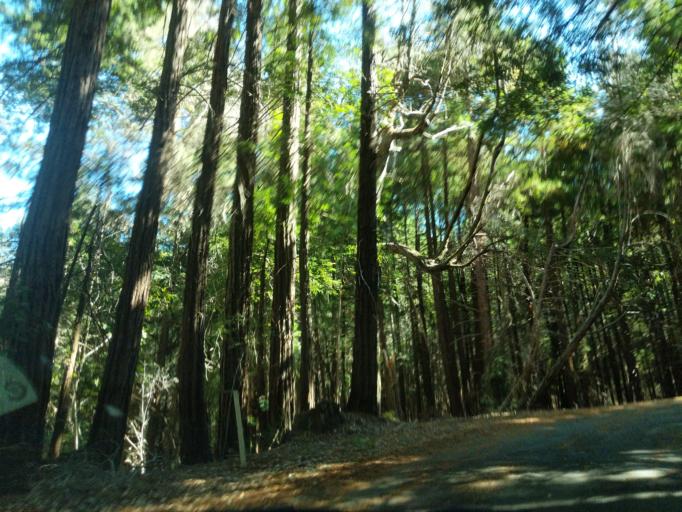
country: US
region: California
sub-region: Sonoma County
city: Monte Rio
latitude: 38.5254
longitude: -123.2357
